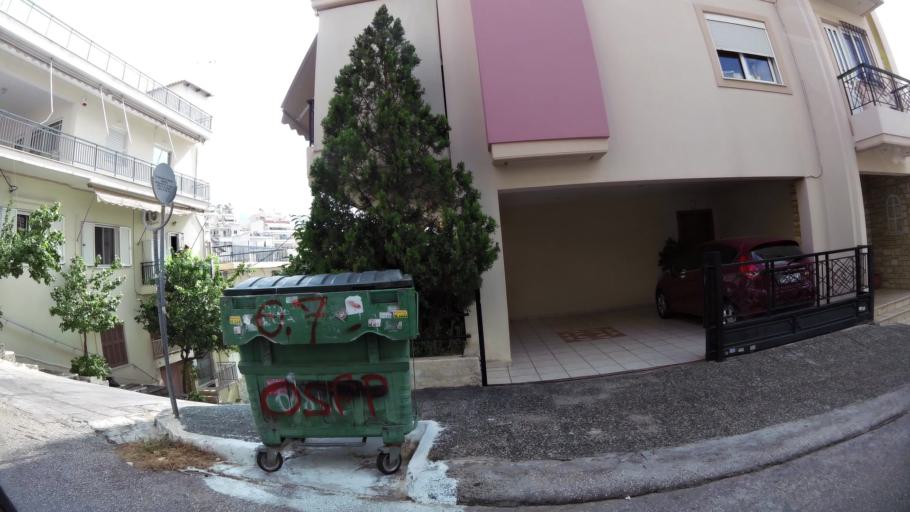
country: GR
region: Attica
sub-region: Nomarchia Athinas
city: Ymittos
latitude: 37.9440
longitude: 23.7601
